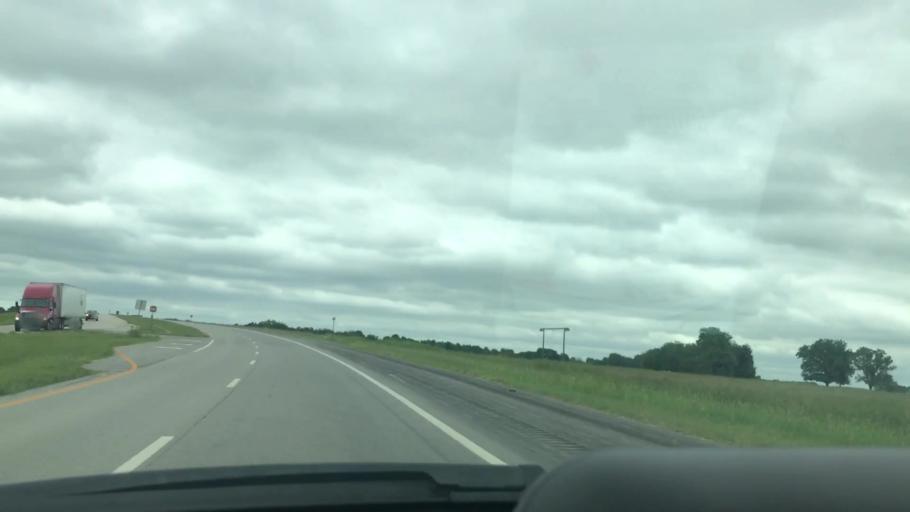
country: US
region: Oklahoma
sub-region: Mayes County
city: Pryor
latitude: 36.3699
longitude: -95.2929
